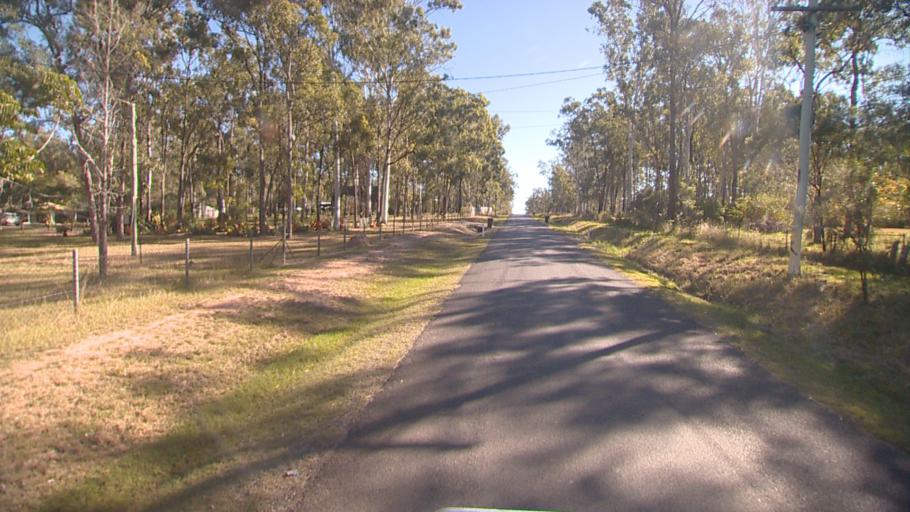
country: AU
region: Queensland
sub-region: Logan
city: Park Ridge South
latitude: -27.7278
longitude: 153.0001
